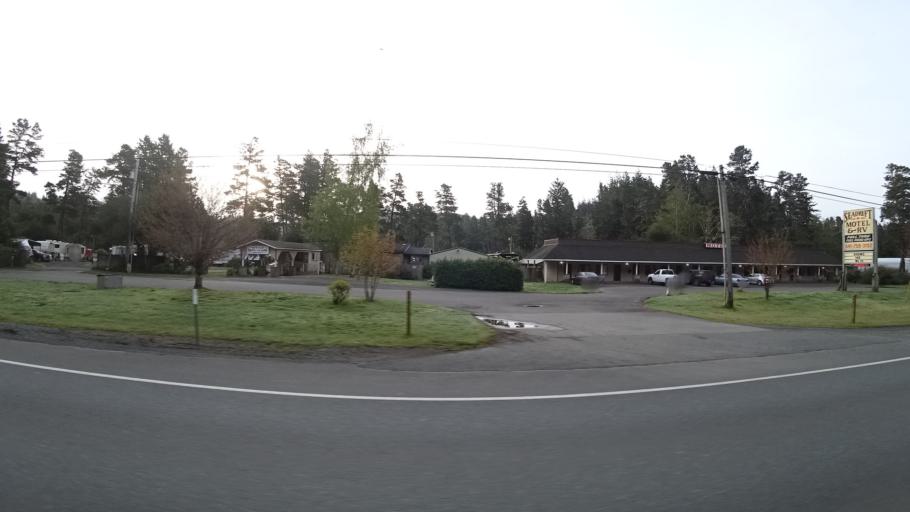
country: US
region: Oregon
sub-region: Coos County
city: Lakeside
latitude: 43.5961
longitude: -124.1812
